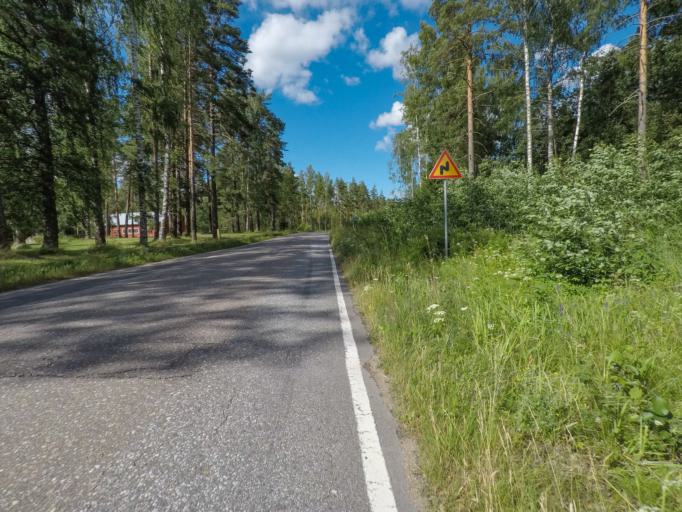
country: FI
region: South Karelia
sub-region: Lappeenranta
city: Joutseno
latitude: 61.1045
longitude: 28.3712
